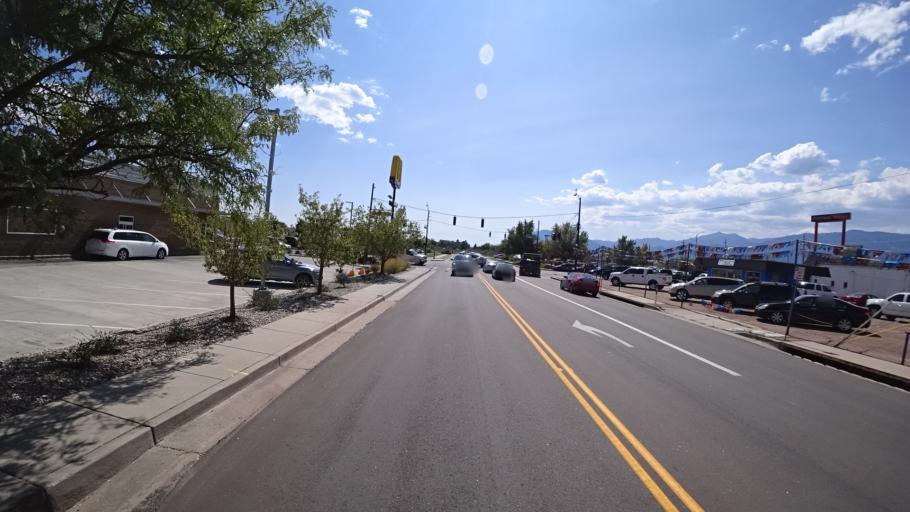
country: US
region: Colorado
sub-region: El Paso County
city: Colorado Springs
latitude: 38.8749
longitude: -104.8162
